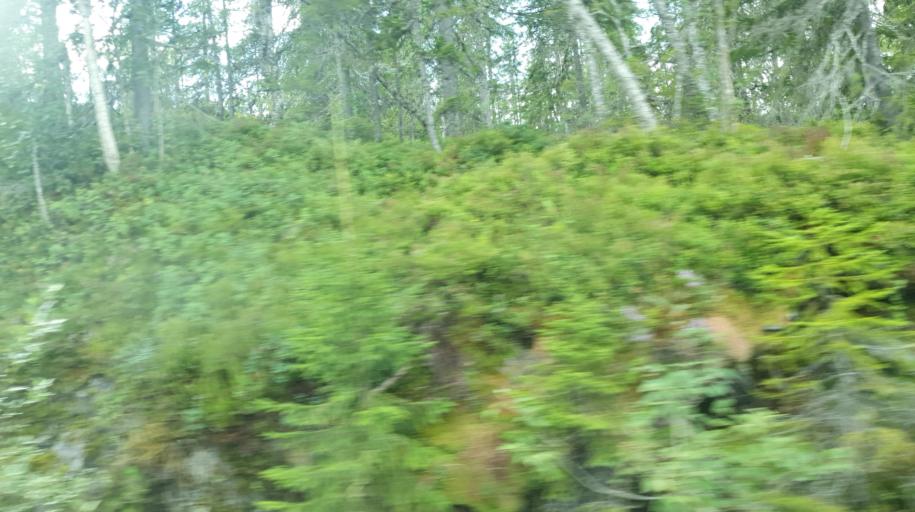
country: NO
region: Nord-Trondelag
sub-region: Levanger
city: Skogn
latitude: 63.5845
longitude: 11.2449
